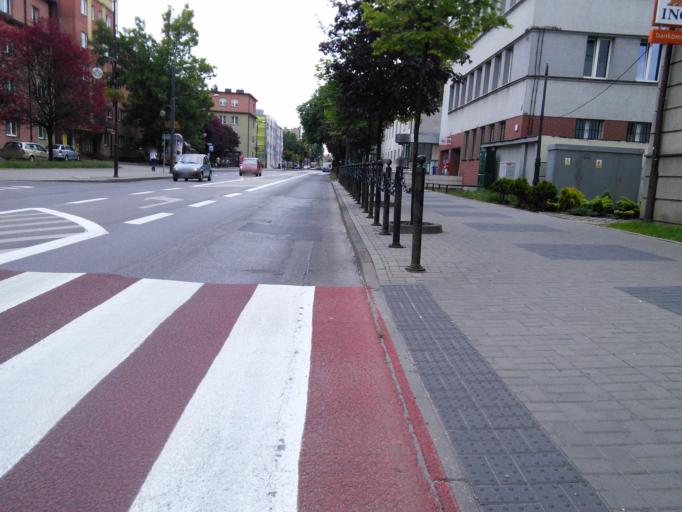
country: PL
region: Silesian Voivodeship
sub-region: Piekary Slaskie
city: Piekary Slaskie
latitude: 50.3758
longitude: 18.9439
